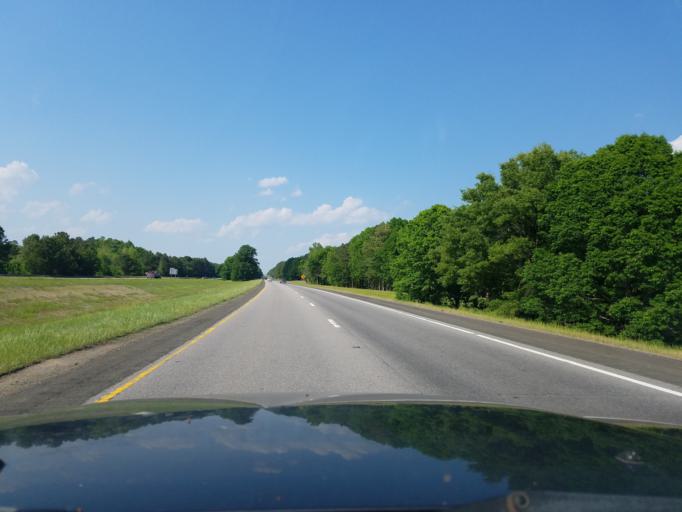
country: US
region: North Carolina
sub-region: Granville County
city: Butner
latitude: 36.0818
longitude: -78.7656
